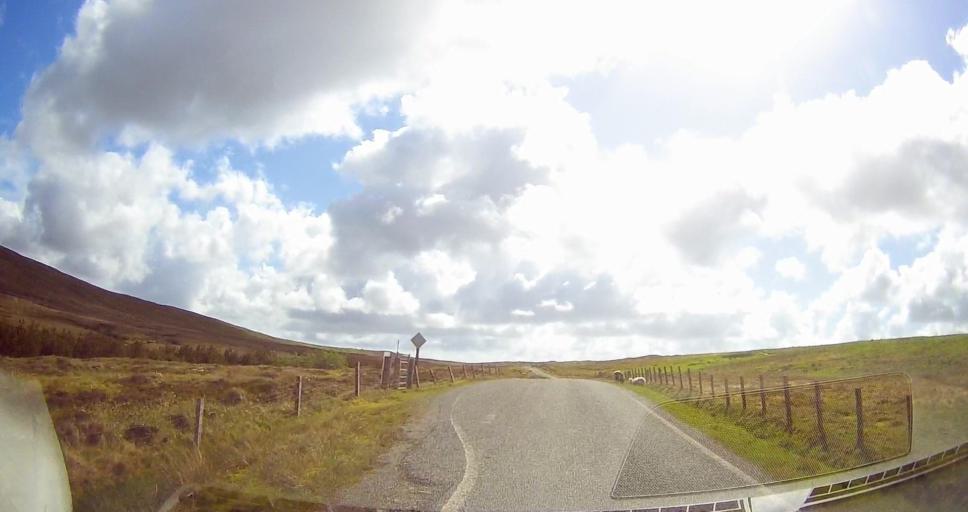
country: GB
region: Scotland
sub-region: Shetland Islands
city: Lerwick
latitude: 60.5075
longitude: -1.3876
